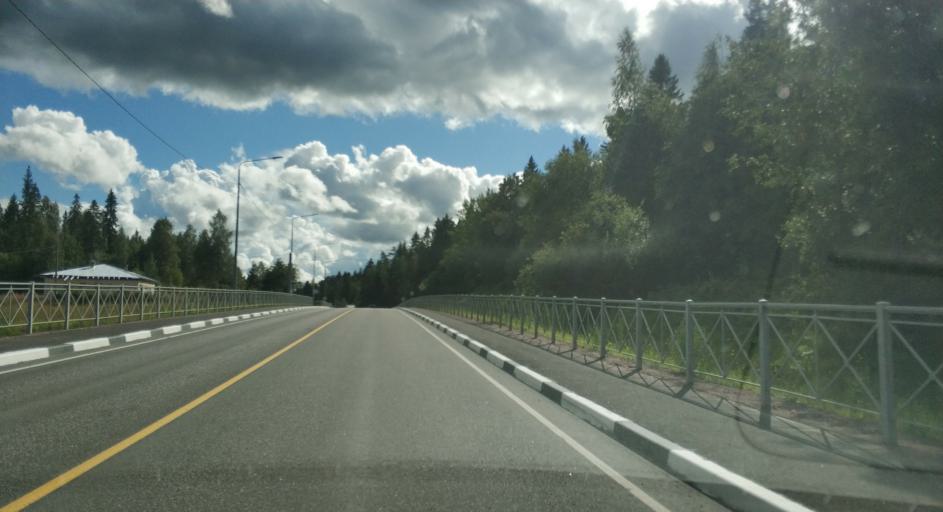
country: RU
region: Republic of Karelia
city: Ruskeala
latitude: 61.9294
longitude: 30.5978
